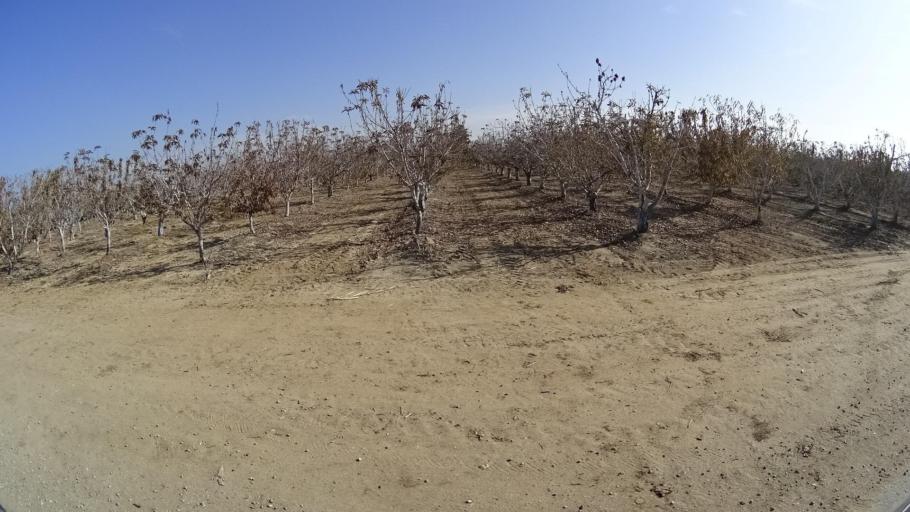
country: US
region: California
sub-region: Kern County
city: McFarland
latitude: 35.6088
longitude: -119.1865
